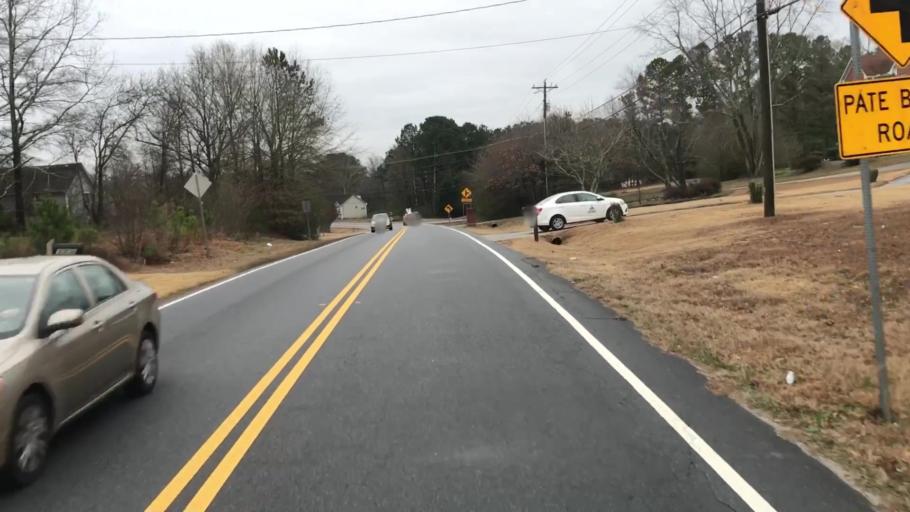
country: US
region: Georgia
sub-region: Gwinnett County
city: Snellville
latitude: 33.8315
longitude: -83.9971
